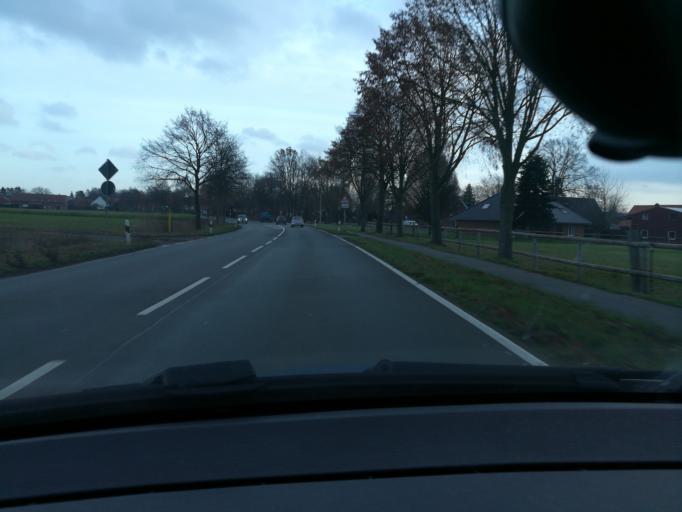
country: DE
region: North Rhine-Westphalia
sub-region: Regierungsbezirk Detmold
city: Hille
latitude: 52.3226
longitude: 8.7832
